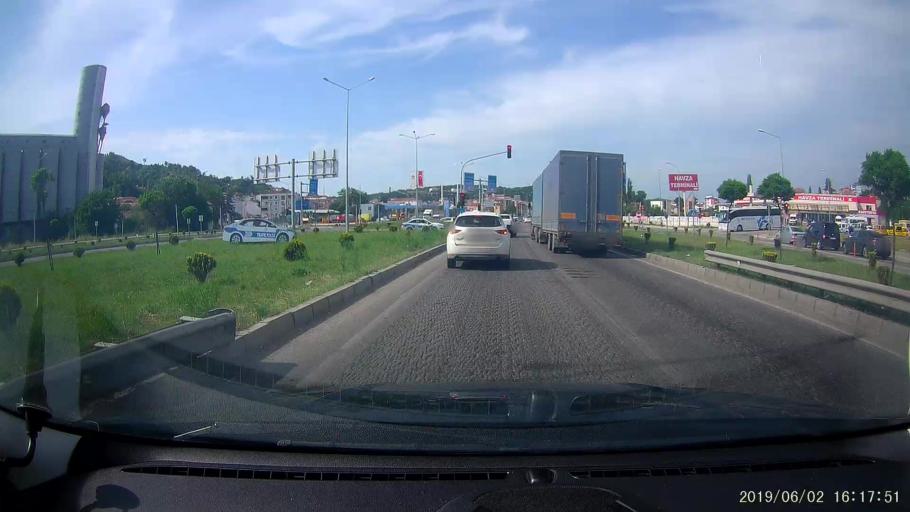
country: TR
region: Samsun
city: Havza
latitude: 40.9609
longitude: 35.6662
